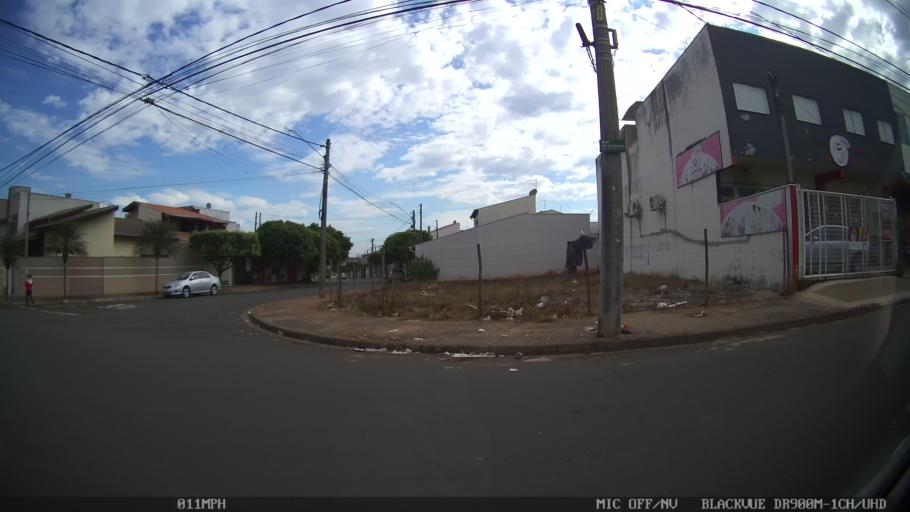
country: BR
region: Sao Paulo
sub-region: Americana
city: Americana
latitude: -22.7328
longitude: -47.3697
